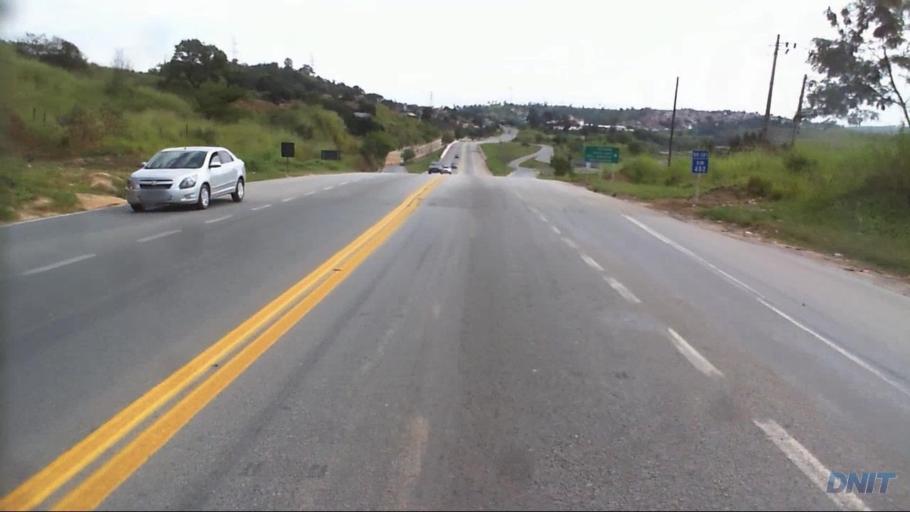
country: BR
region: Minas Gerais
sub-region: Santa Luzia
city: Santa Luzia
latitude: -19.8343
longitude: -43.8520
